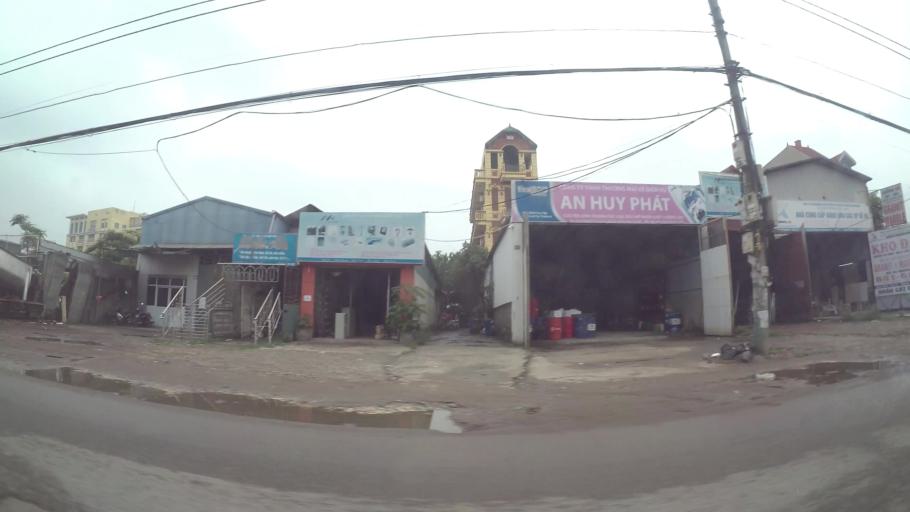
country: VN
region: Ha Noi
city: Van Dien
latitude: 20.9775
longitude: 105.8653
